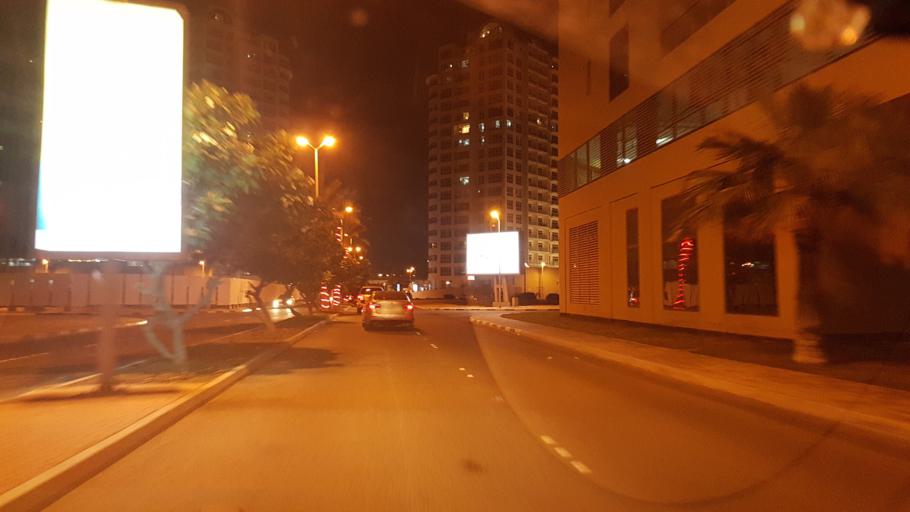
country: BH
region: Muharraq
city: Al Hadd
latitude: 26.2925
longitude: 50.6655
